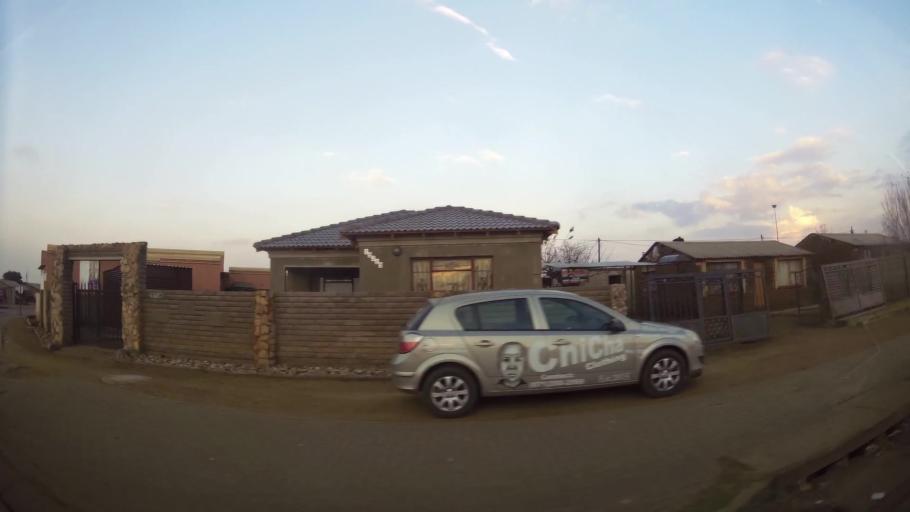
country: ZA
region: Gauteng
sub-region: City of Johannesburg Metropolitan Municipality
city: Orange Farm
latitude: -26.5508
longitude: 27.8642
